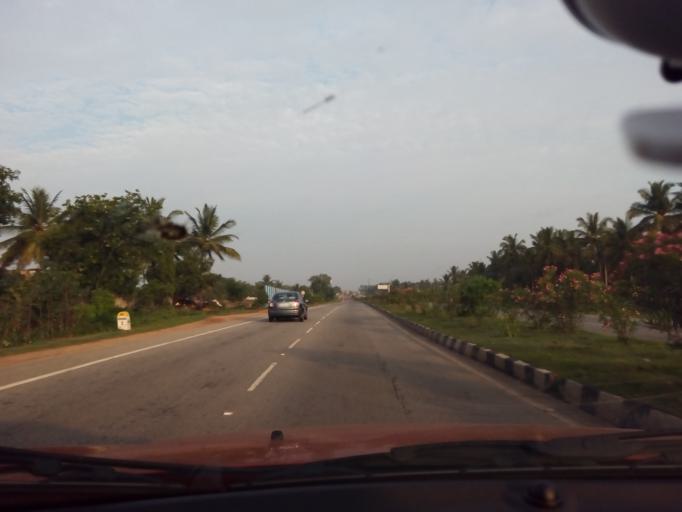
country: IN
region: Karnataka
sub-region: Ramanagara
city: Magadi
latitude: 13.0640
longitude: 77.2613
